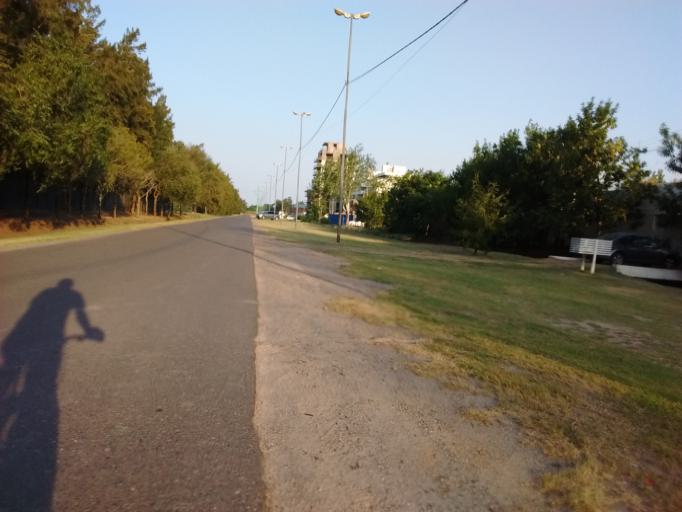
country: AR
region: Santa Fe
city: Funes
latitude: -32.9145
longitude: -60.7569
